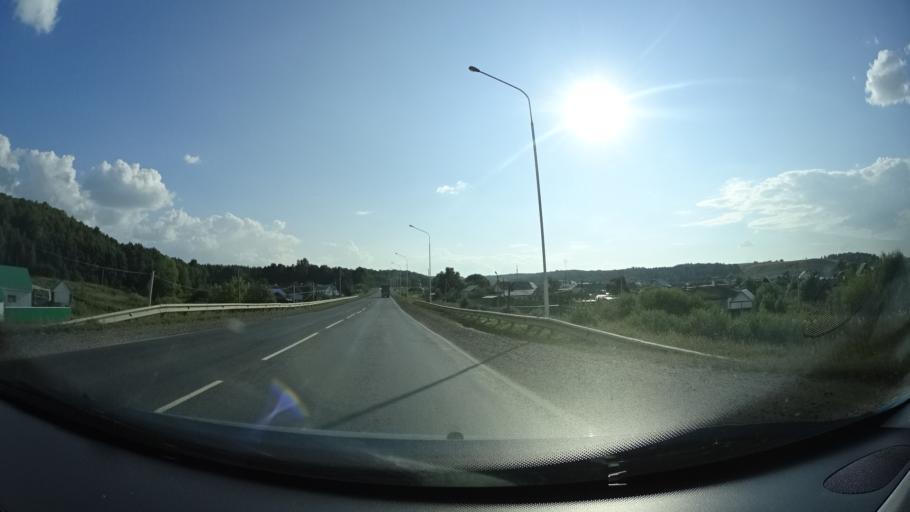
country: RU
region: Tatarstan
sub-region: Bavlinskiy Rayon
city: Bavly
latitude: 54.4599
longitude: 53.2821
